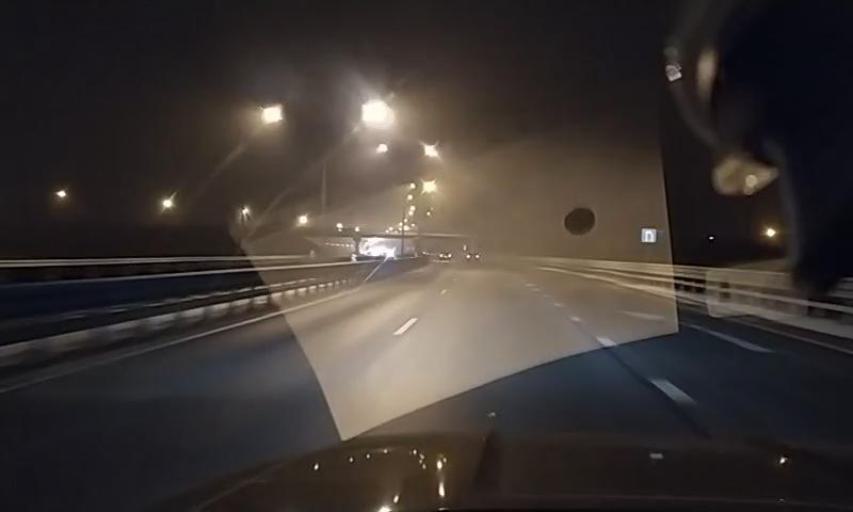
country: RU
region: Leningrad
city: Bugry
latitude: 60.0993
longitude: 30.3832
